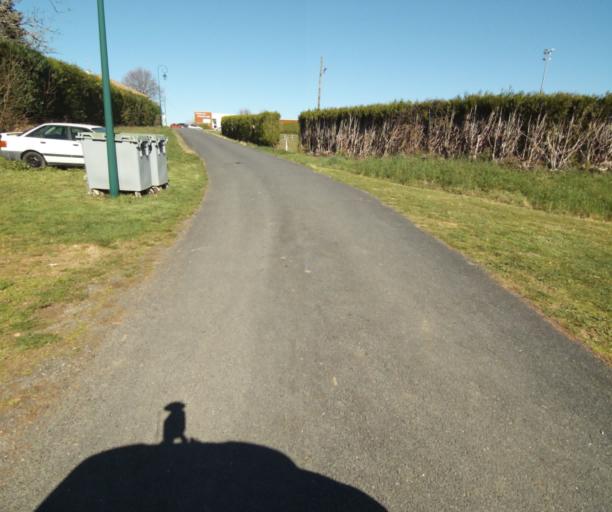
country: FR
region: Limousin
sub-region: Departement de la Correze
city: Seilhac
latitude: 45.3662
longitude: 1.7221
